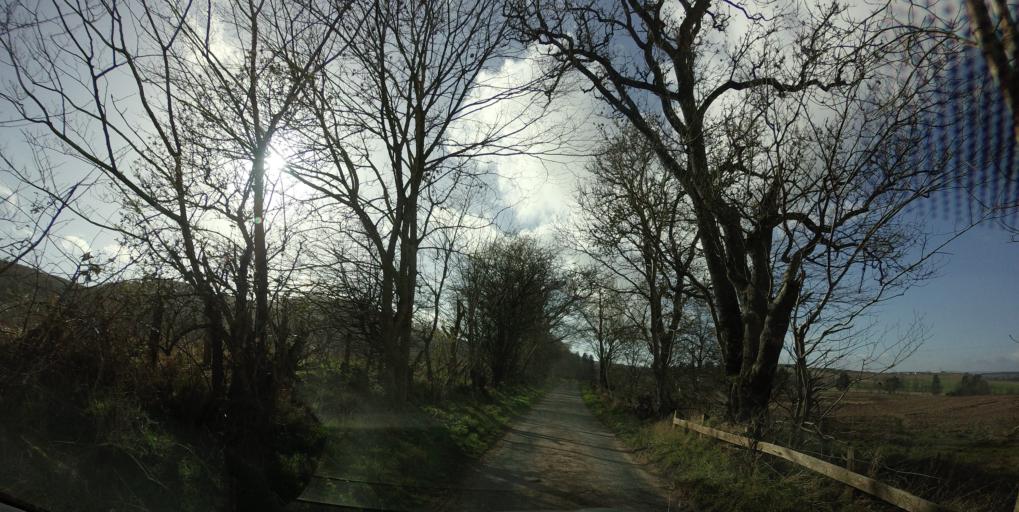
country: GB
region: Scotland
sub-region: Perth and Kinross
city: Bridge of Earn
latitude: 56.3307
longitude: -3.4255
